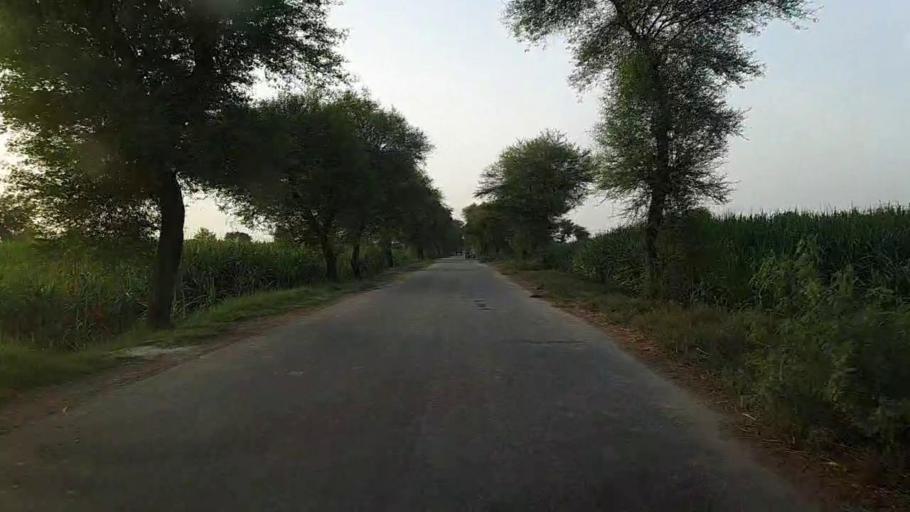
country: PK
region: Sindh
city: Ubauro
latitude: 28.2331
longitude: 69.8152
